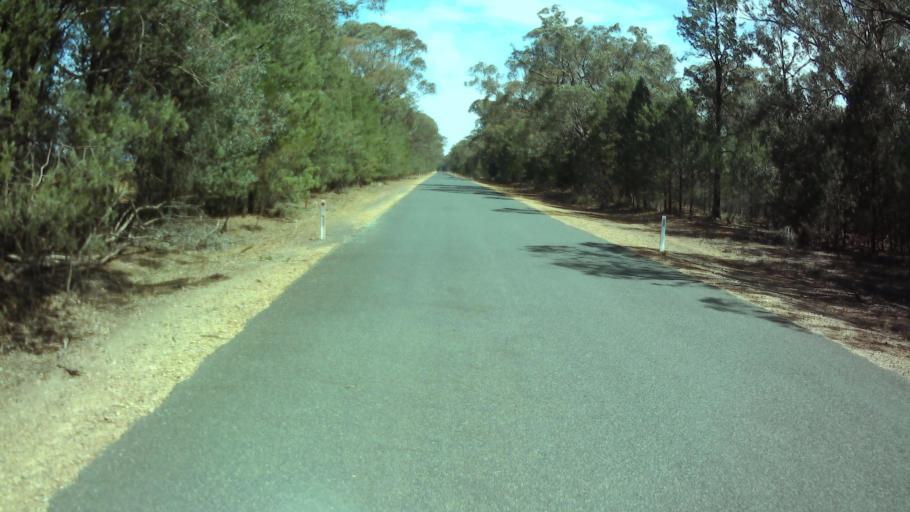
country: AU
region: New South Wales
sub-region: Weddin
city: Grenfell
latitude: -34.0146
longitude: 148.1288
